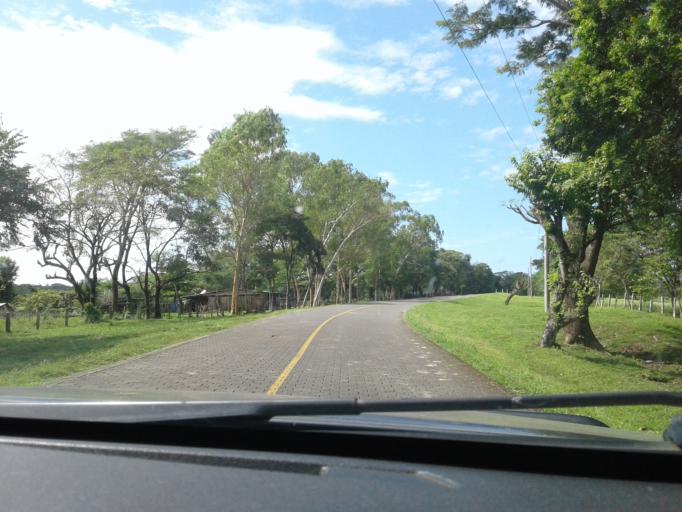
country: NI
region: Rivas
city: Cardenas
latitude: 11.1715
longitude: -85.4762
